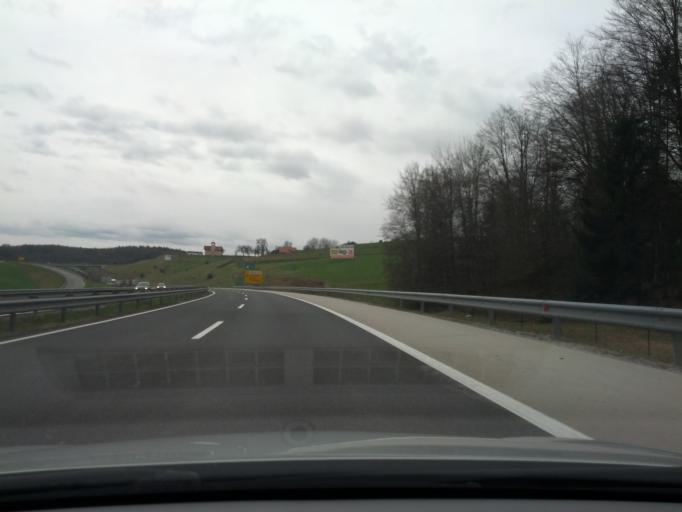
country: SI
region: Trebnje
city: Trebnje
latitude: 45.9150
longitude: 14.9563
